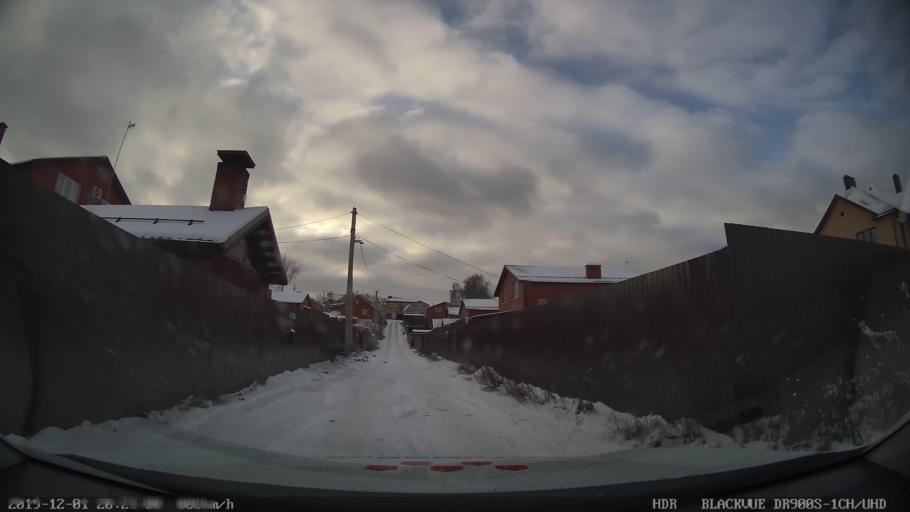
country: RU
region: Tatarstan
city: Stolbishchi
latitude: 55.7451
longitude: 49.2703
